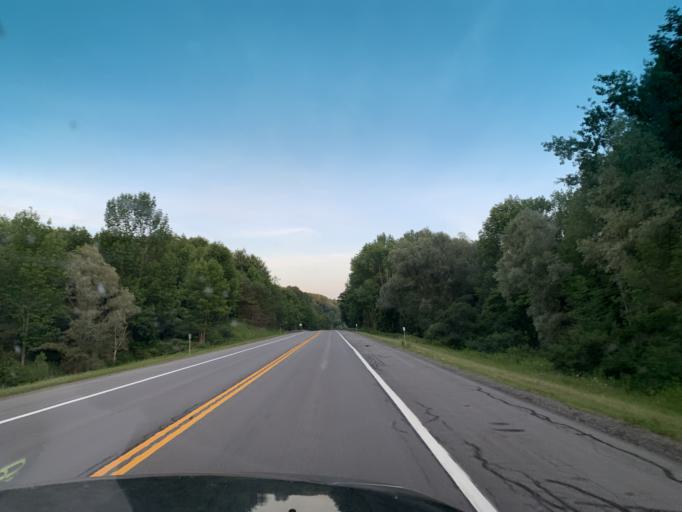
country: US
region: New York
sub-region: Oneida County
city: Chadwicks
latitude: 42.9660
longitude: -75.2501
